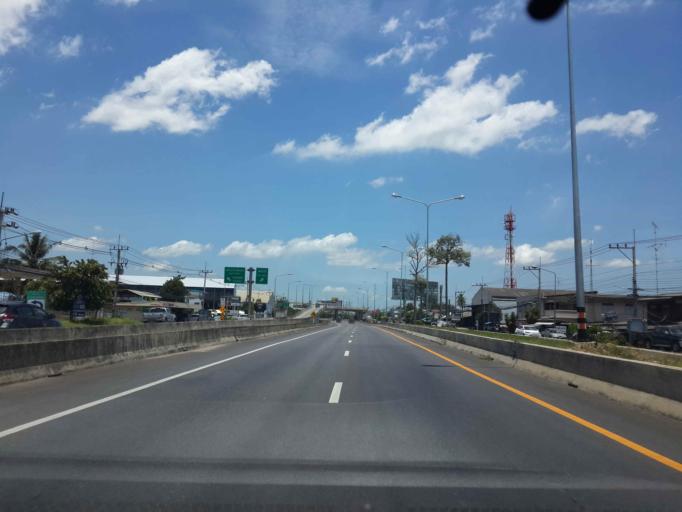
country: TH
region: Phetchaburi
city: Ban Lat
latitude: 13.0723
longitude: 99.9475
